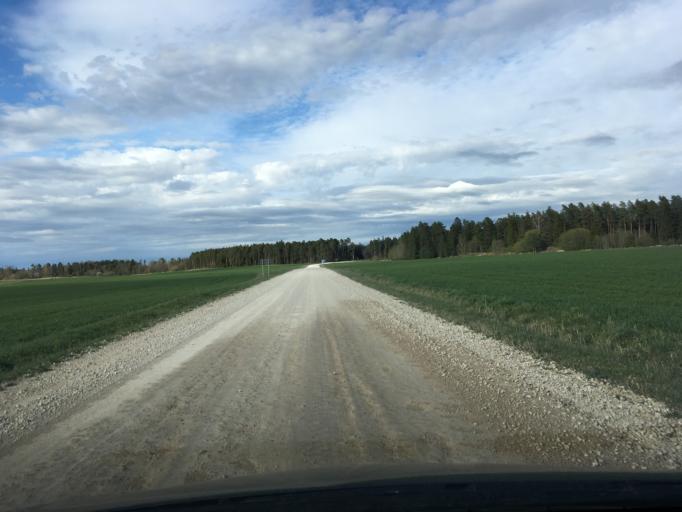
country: EE
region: Raplamaa
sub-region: Maerjamaa vald
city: Marjamaa
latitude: 59.0060
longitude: 24.3927
